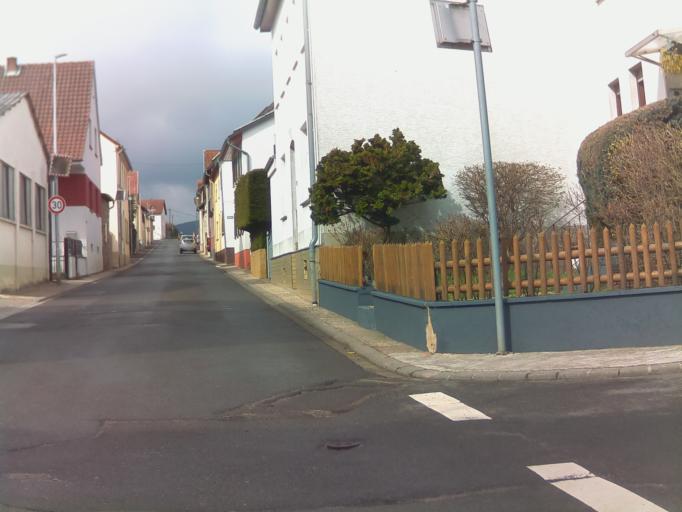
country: DE
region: Rheinland-Pfalz
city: Dorrebach
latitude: 49.9453
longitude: 7.7199
